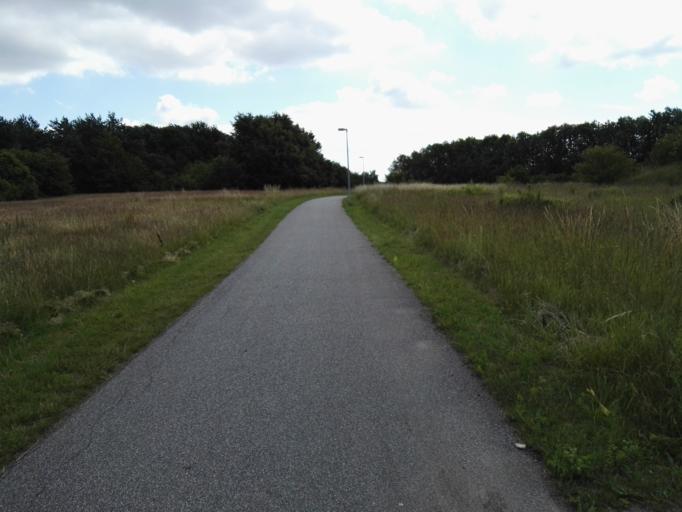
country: DK
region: Capital Region
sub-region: Ballerup Kommune
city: Ballerup
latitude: 55.7339
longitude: 12.3964
